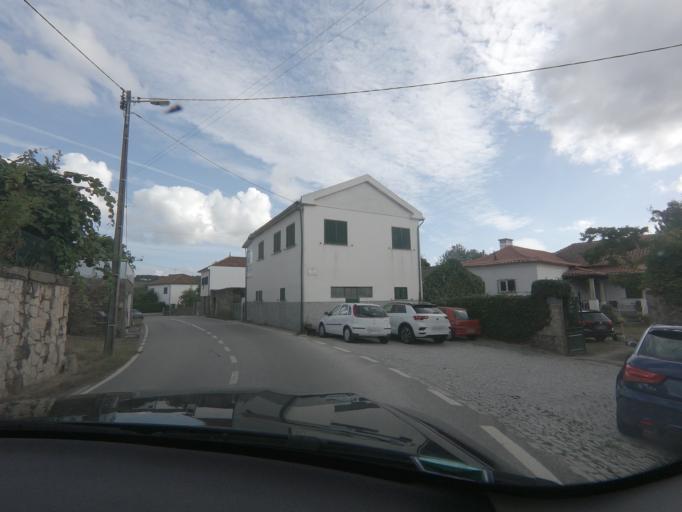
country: PT
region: Vila Real
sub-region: Vila Real
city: Vila Real
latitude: 41.2675
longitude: -7.7061
